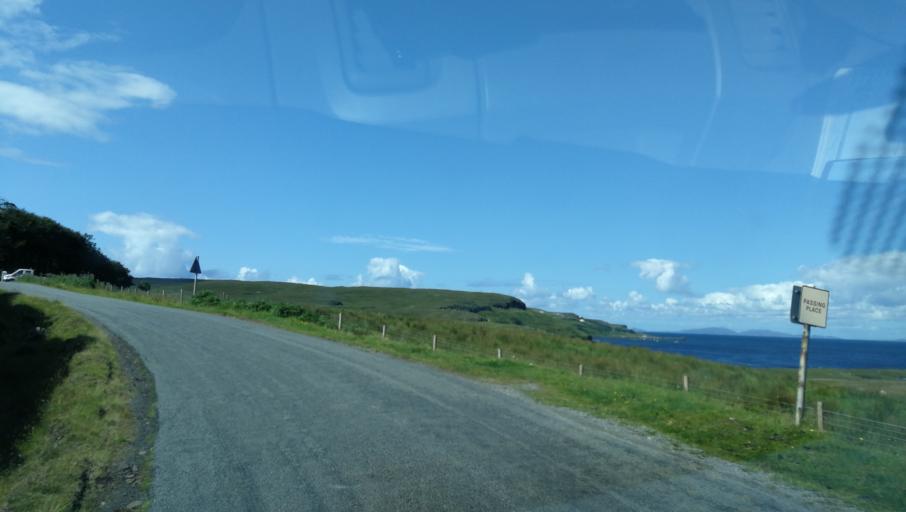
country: GB
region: Scotland
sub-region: Eilean Siar
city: Harris
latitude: 57.4486
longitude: -6.7145
